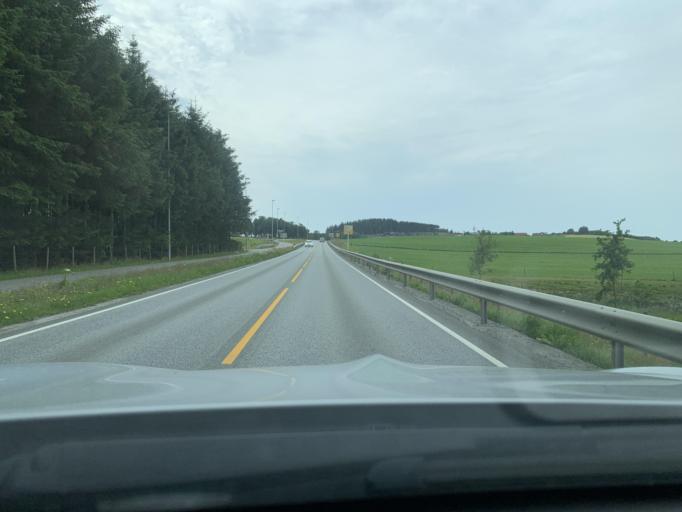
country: NO
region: Rogaland
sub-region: Time
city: Bryne
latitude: 58.7365
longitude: 5.6851
